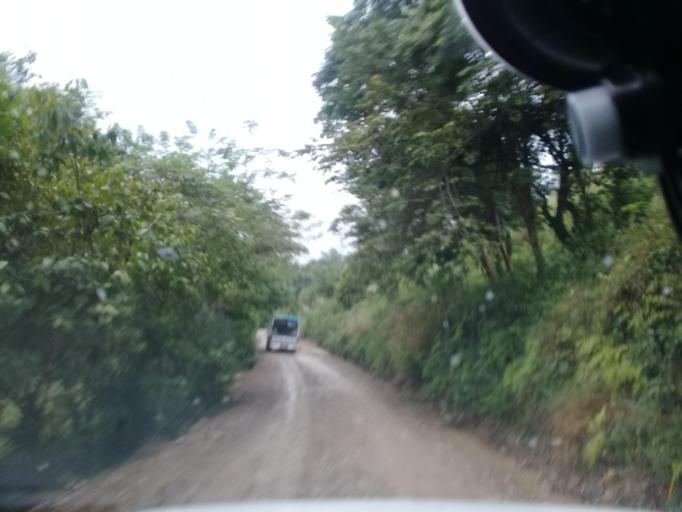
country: MX
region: Veracruz
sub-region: Chalma
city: San Pedro Coyutla
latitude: 21.2316
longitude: -98.4209
